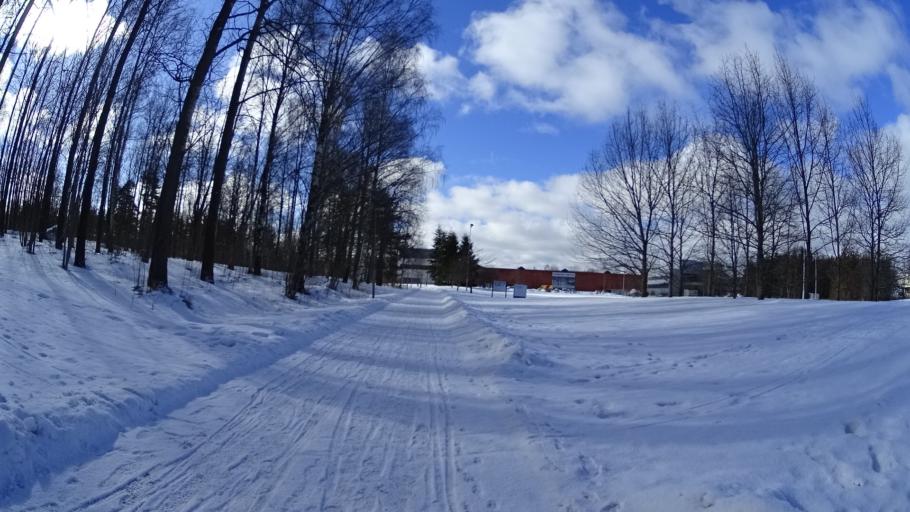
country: FI
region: Uusimaa
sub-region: Helsinki
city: Teekkarikylae
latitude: 60.2408
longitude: 24.8587
